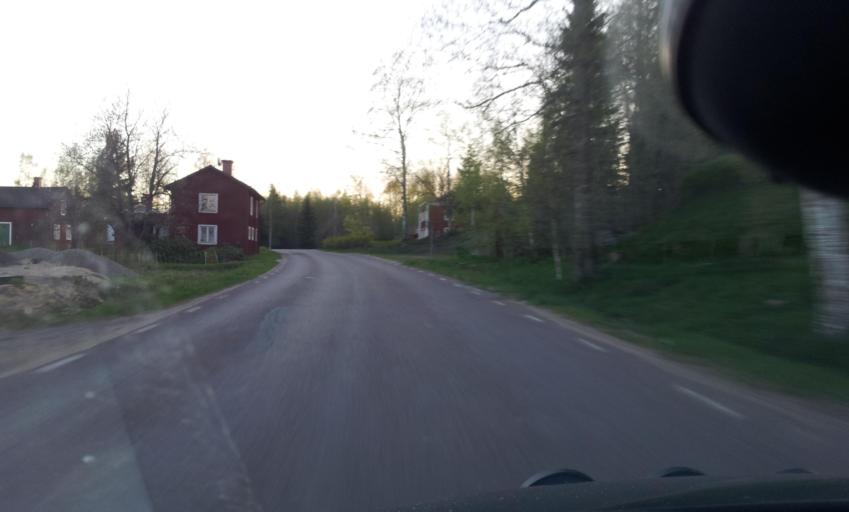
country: SE
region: Gaevleborg
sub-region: Bollnas Kommun
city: Bollnas
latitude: 61.4032
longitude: 16.5154
